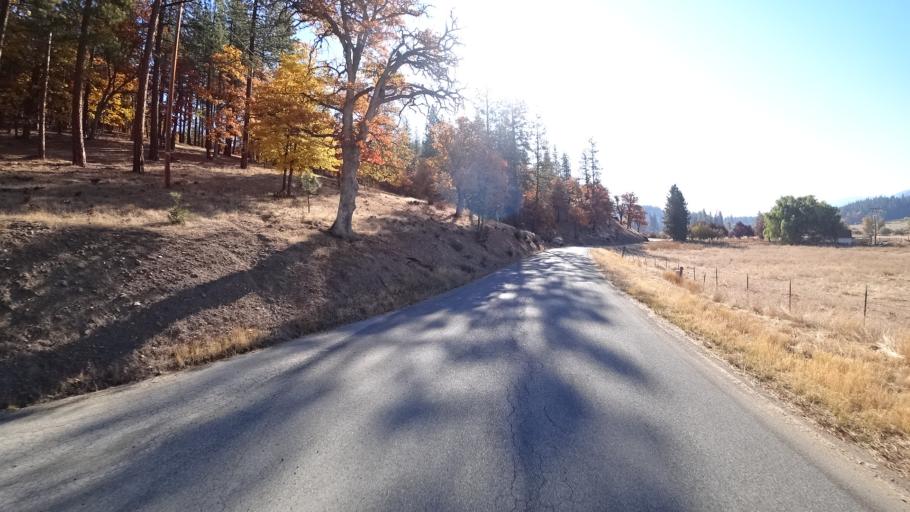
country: US
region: California
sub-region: Siskiyou County
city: Yreka
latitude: 41.6405
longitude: -122.9882
